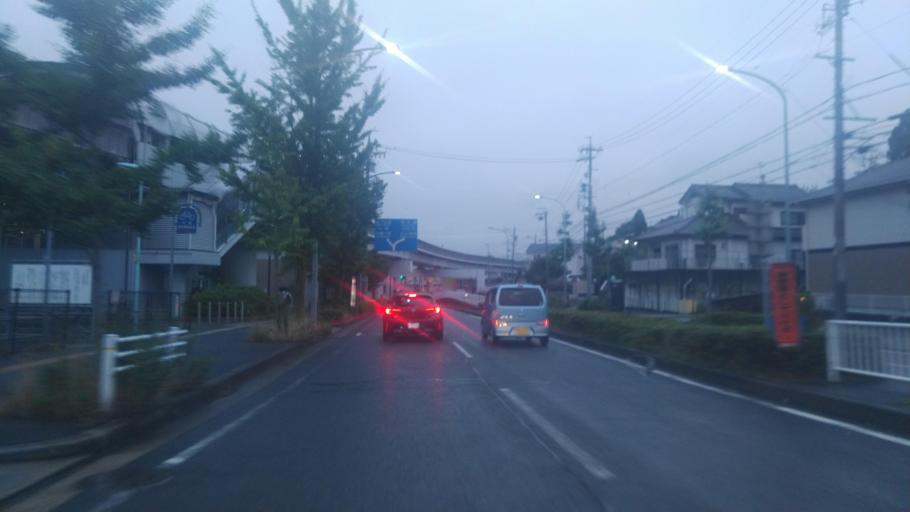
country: JP
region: Aichi
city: Kasugai
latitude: 35.2192
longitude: 136.9829
